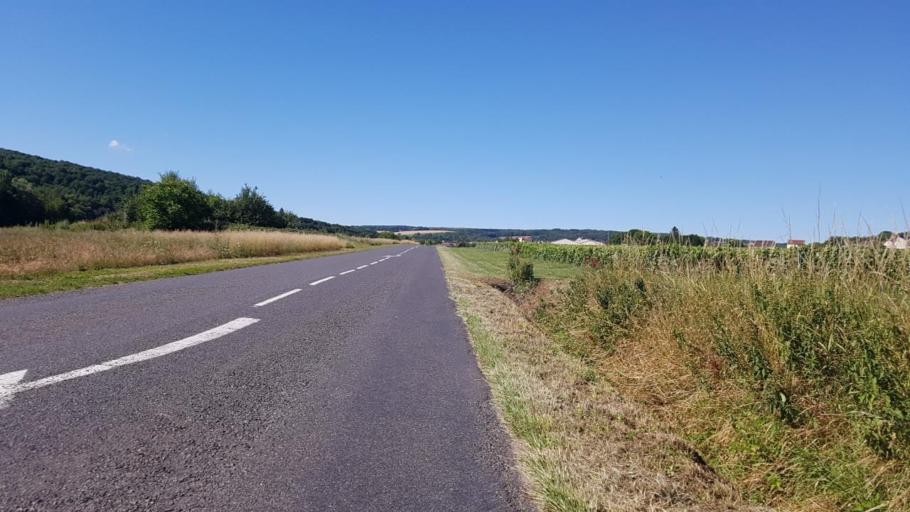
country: FR
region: Picardie
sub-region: Departement de l'Aisne
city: Chezy-sur-Marne
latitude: 48.9811
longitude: 3.3411
